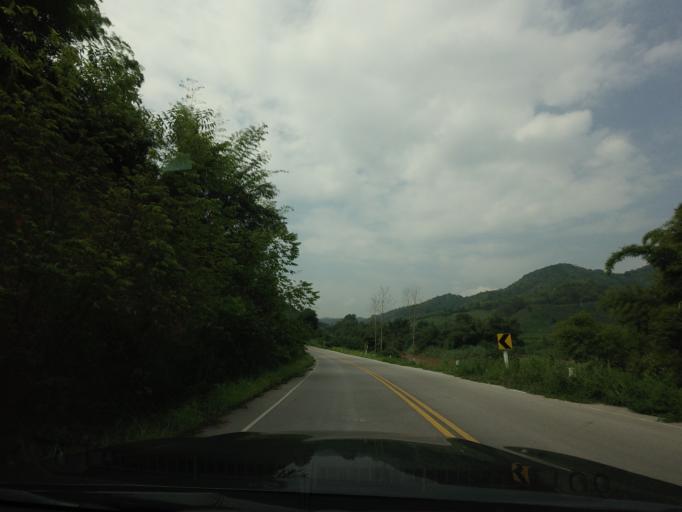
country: LA
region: Xiagnabouli
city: Muang Kenthao
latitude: 17.7673
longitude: 101.5151
